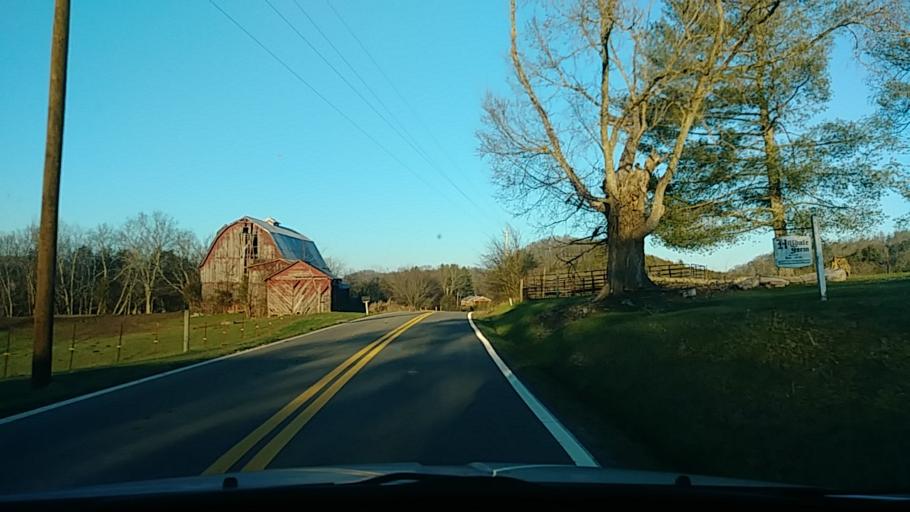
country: US
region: Tennessee
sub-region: Greene County
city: Mosheim
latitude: 36.1214
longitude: -83.0665
